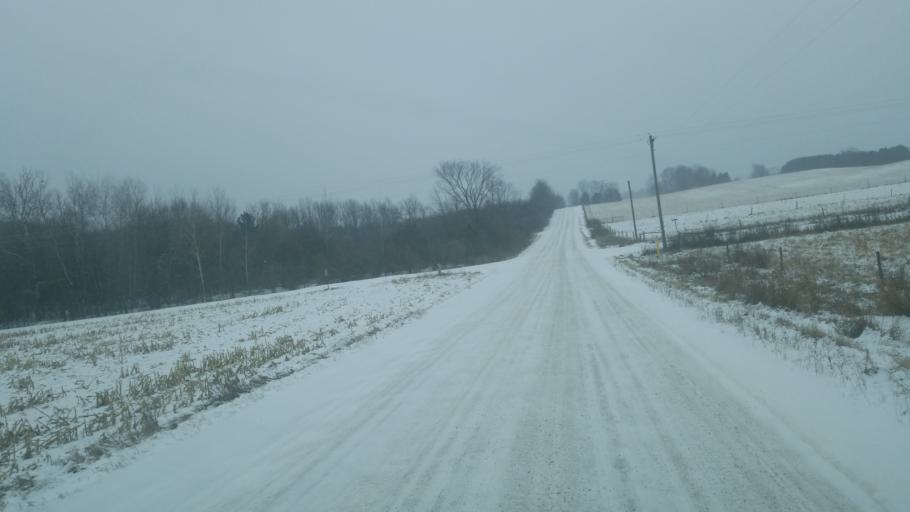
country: US
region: Michigan
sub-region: Osceola County
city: Reed City
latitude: 43.8295
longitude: -85.3938
